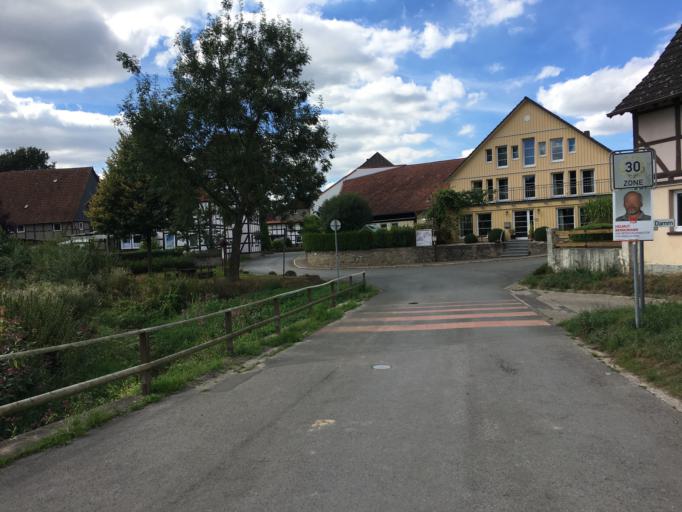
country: DE
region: Lower Saxony
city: Ottenstein
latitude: 52.0119
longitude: 9.3451
